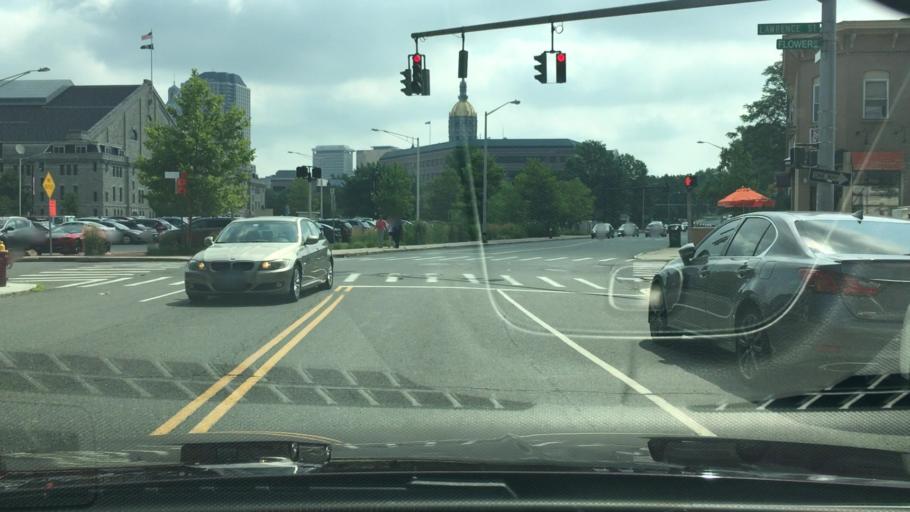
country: US
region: Connecticut
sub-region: Hartford County
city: Hartford
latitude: 41.7639
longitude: -72.6882
